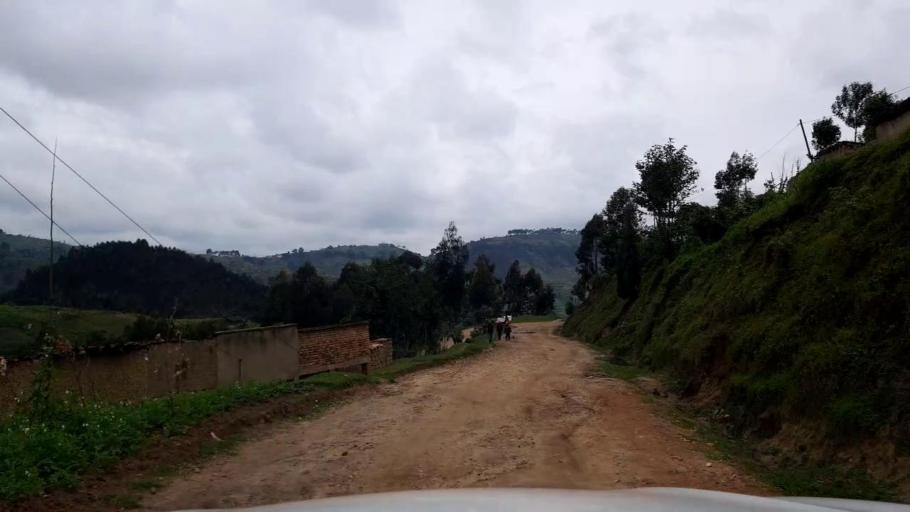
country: RW
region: Western Province
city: Kibuye
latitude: -1.9575
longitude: 29.4231
